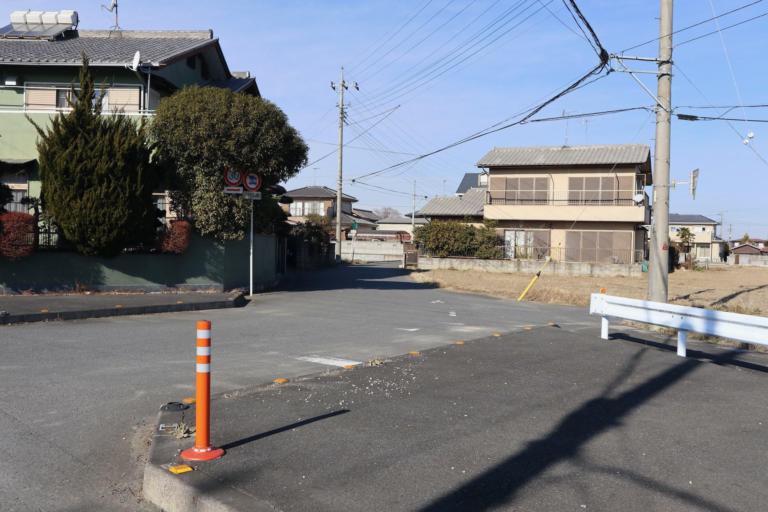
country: JP
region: Saitama
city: Fukiage-fujimi
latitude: 36.0912
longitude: 139.4451
